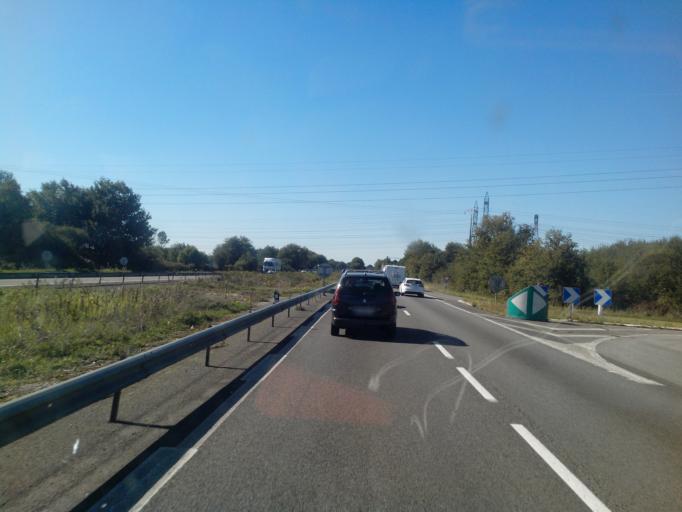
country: FR
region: Pays de la Loire
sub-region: Departement de la Loire-Atlantique
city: Malville
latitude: 47.3412
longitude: -1.8300
